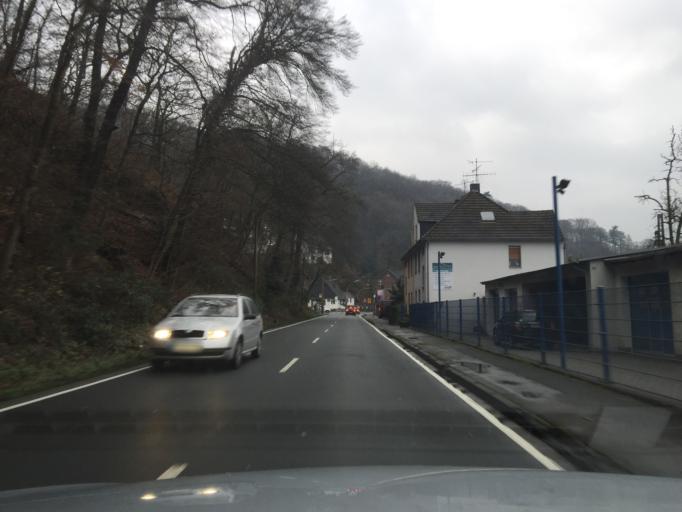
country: DE
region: North Rhine-Westphalia
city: Wetter (Ruhr)
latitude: 51.3767
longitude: 7.3823
